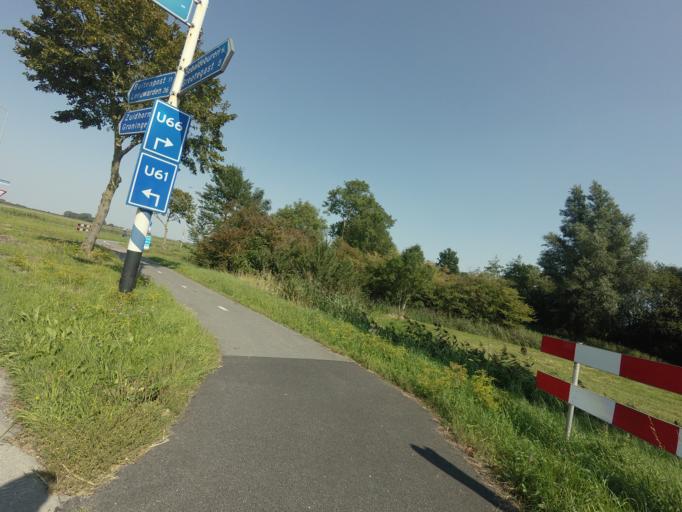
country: NL
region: Groningen
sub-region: Gemeente Zuidhorn
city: Grijpskerk
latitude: 53.2637
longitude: 6.3193
